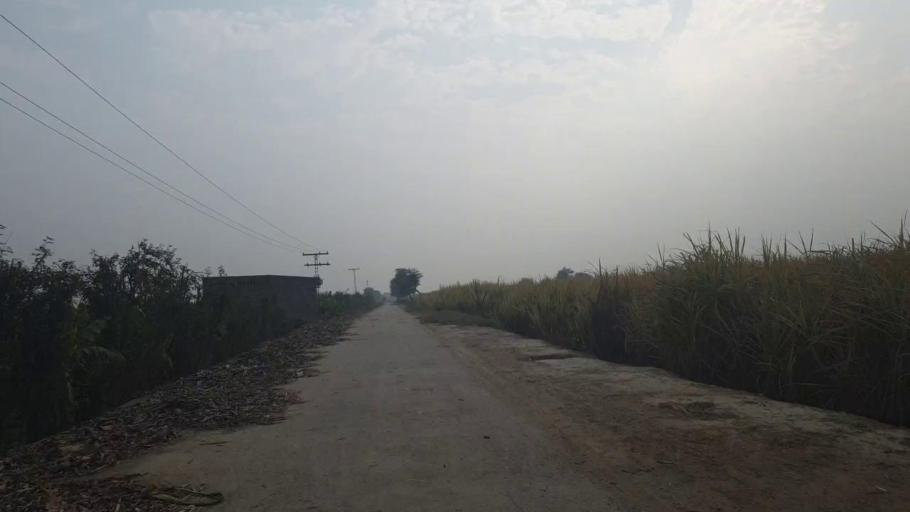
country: PK
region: Sindh
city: Berani
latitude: 25.8061
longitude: 68.7328
